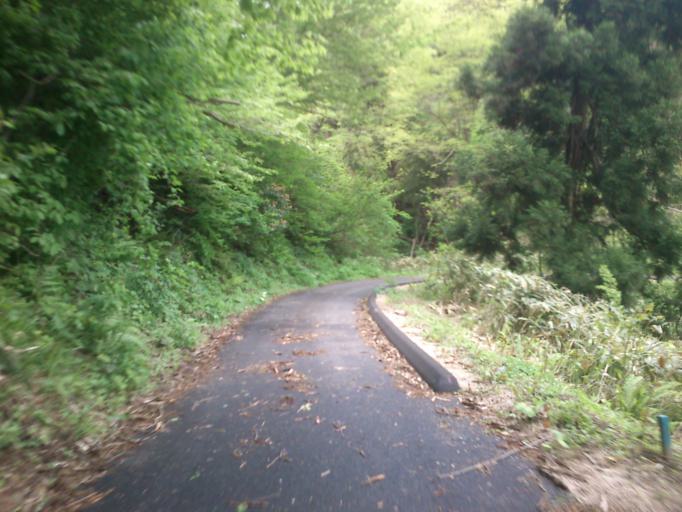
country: JP
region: Kyoto
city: Miyazu
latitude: 35.6490
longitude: 135.1560
